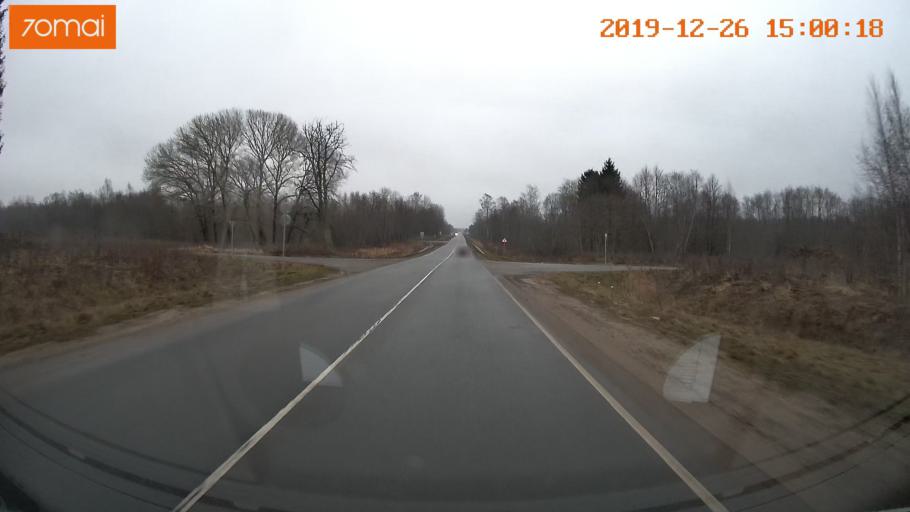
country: RU
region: Jaroslavl
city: Rybinsk
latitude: 58.2477
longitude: 38.8498
